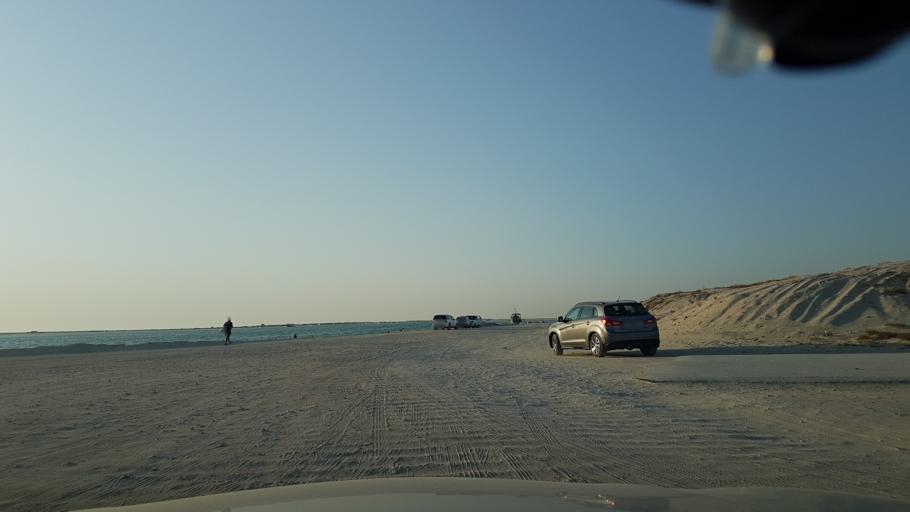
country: BH
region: Manama
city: Jidd Hafs
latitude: 26.2456
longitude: 50.5028
